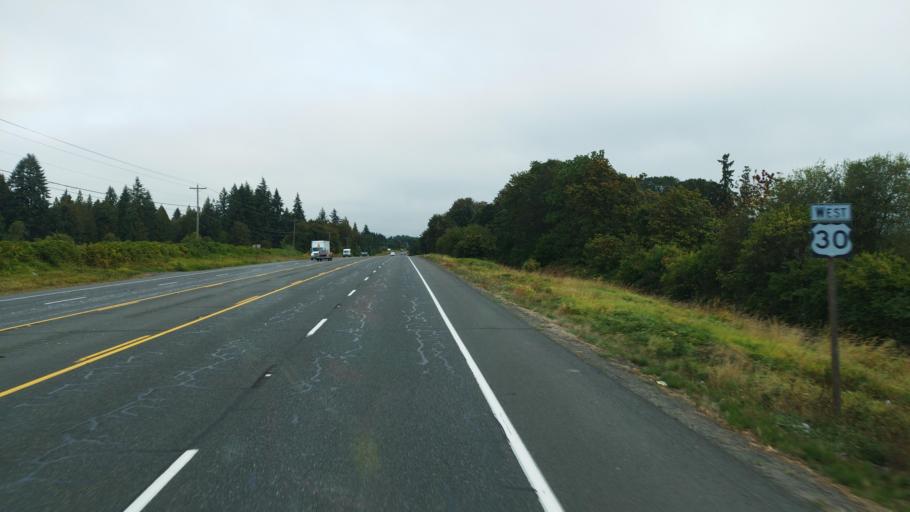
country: US
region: Oregon
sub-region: Columbia County
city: Warren
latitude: 45.7924
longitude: -122.8688
